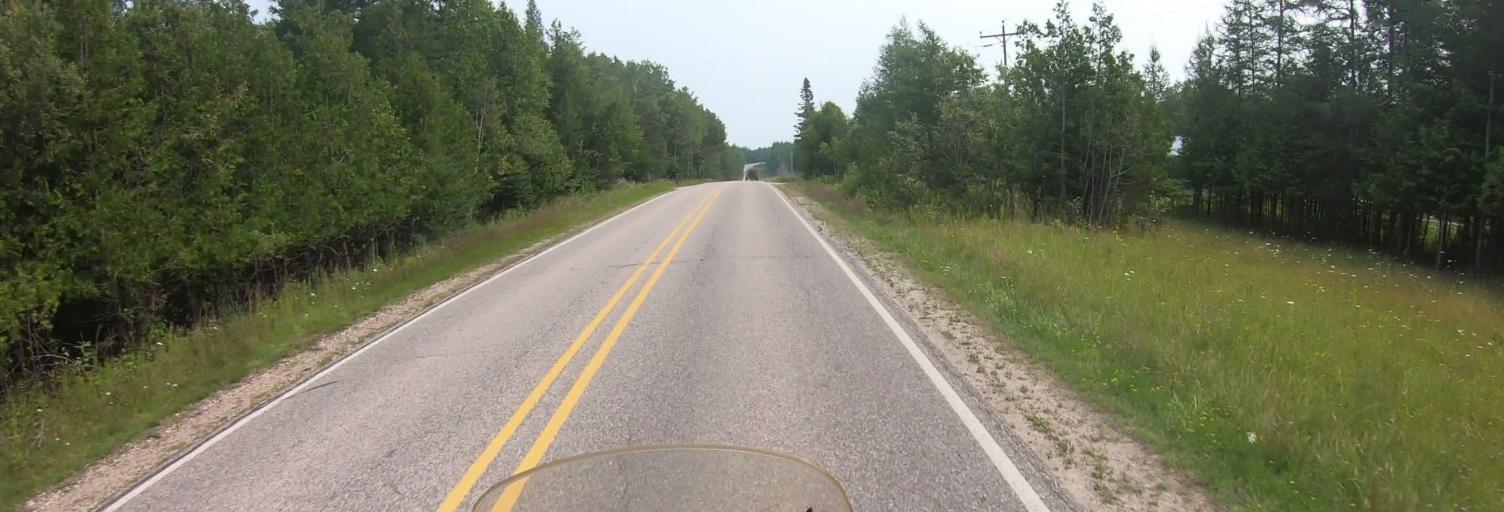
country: CA
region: Ontario
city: Thessalon
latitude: 45.9987
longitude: -83.7178
